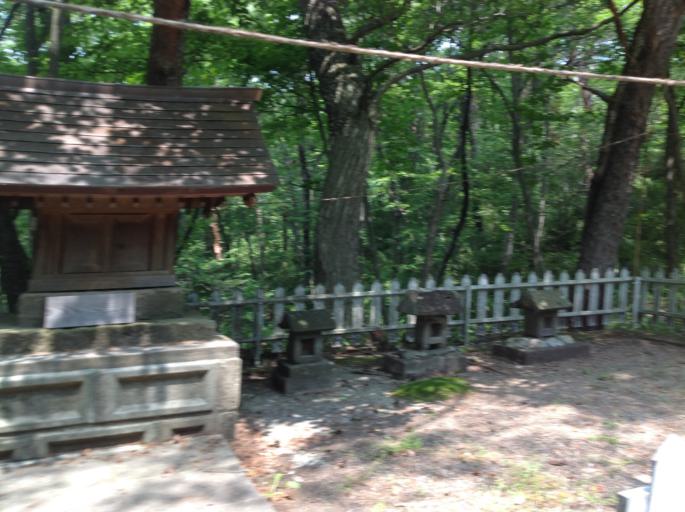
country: JP
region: Iwate
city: Ichinoseki
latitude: 38.9405
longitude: 141.1228
